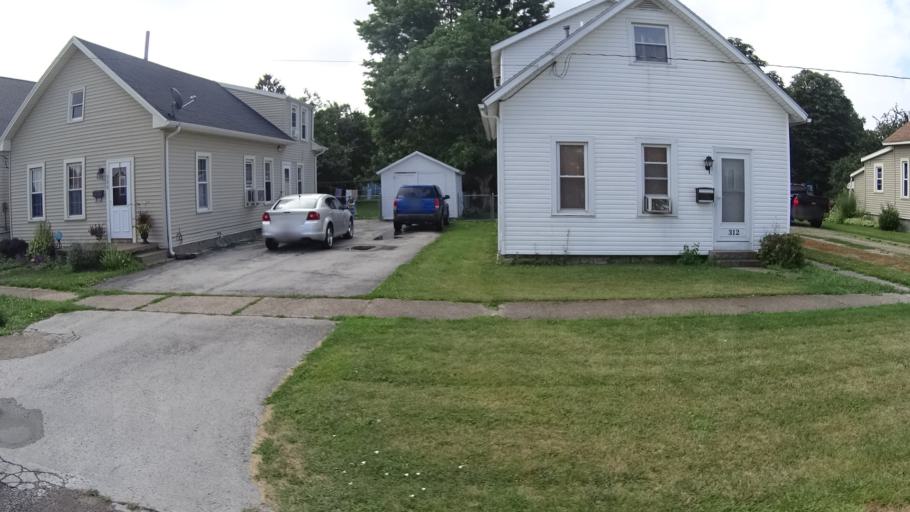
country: US
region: Ohio
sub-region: Erie County
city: Sandusky
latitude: 41.4360
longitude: -82.7044
